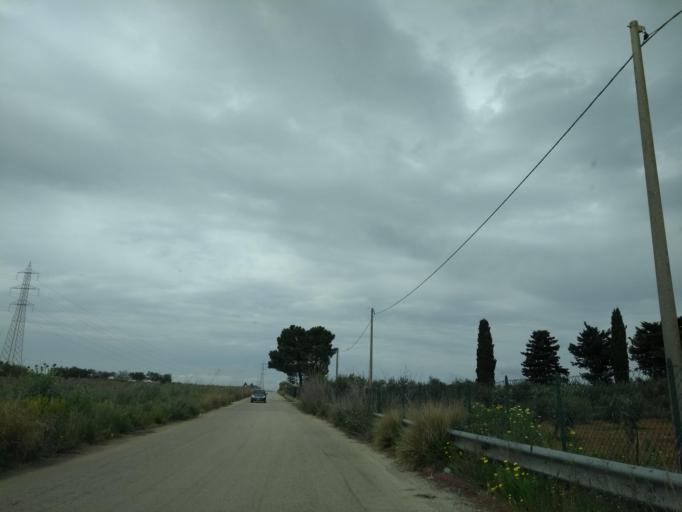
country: IT
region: Sicily
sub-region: Palermo
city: Partinico
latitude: 37.9909
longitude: 13.0682
